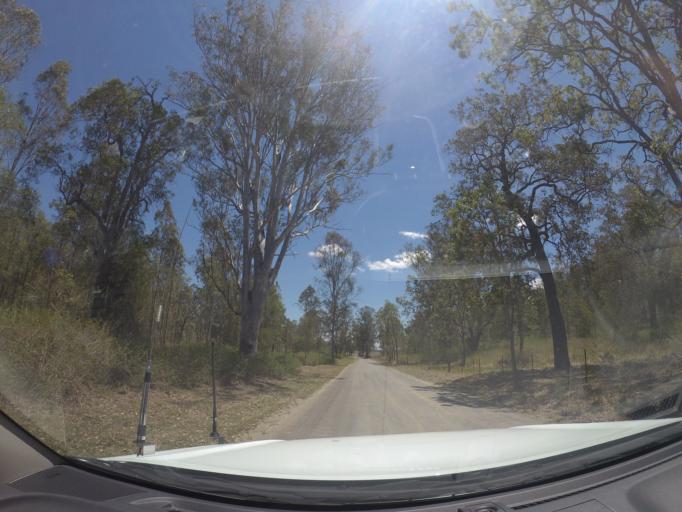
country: AU
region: Queensland
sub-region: Ipswich
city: Redbank Plains
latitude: -27.7551
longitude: 152.8355
